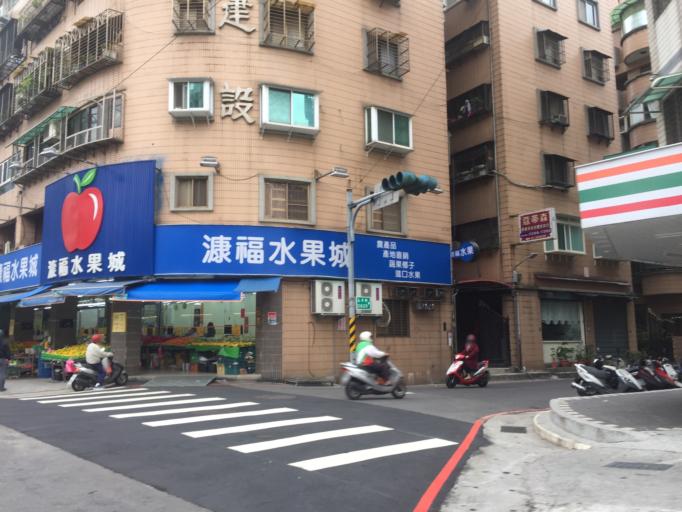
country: TW
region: Taipei
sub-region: Taipei
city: Banqiao
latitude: 25.0921
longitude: 121.4604
